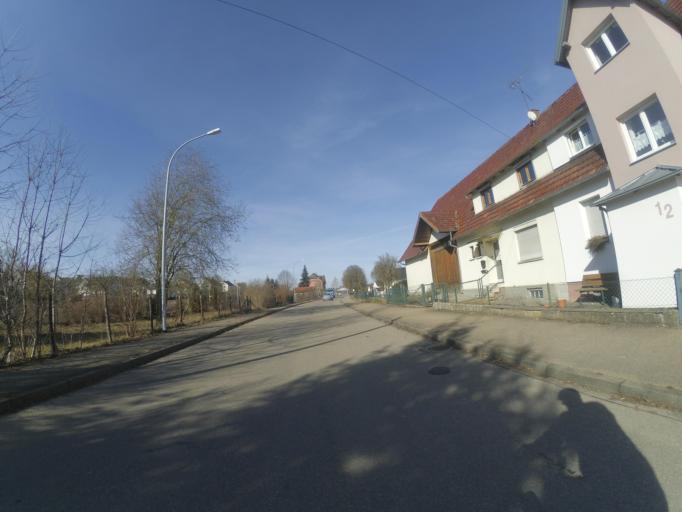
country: DE
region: Baden-Wuerttemberg
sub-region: Regierungsbezirk Stuttgart
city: Sontheim an der Brenz
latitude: 48.5578
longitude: 10.2856
